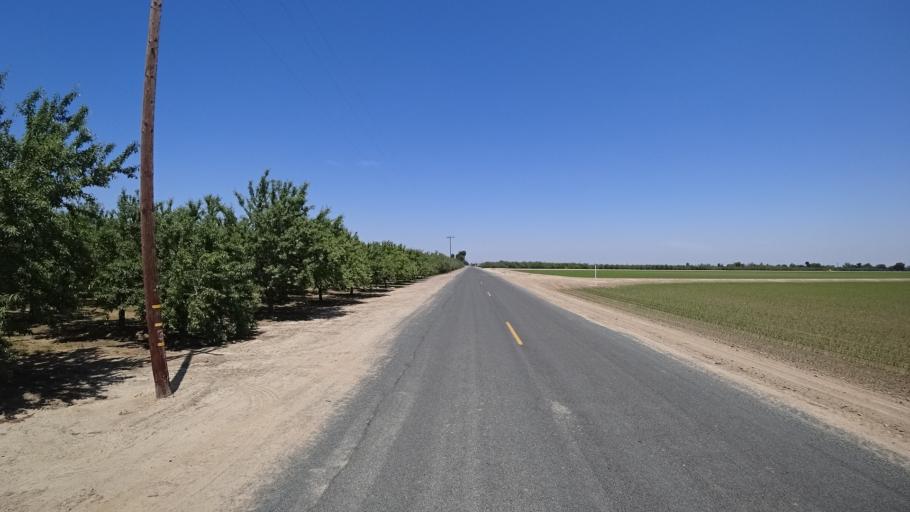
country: US
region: California
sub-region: Kings County
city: Armona
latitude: 36.2649
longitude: -119.7269
